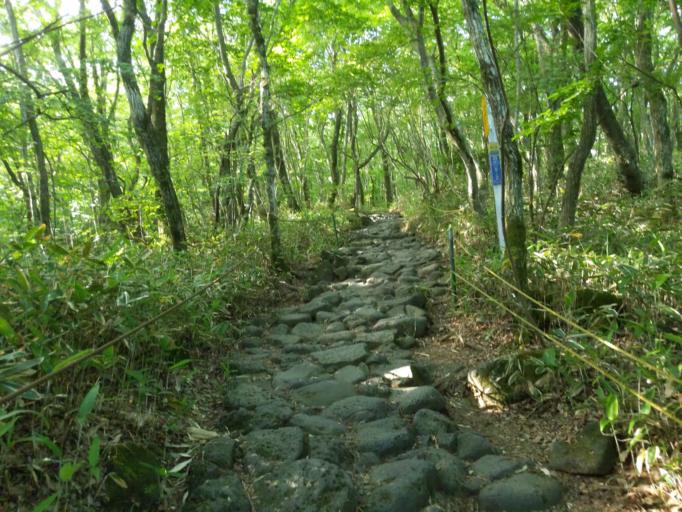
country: KR
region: Jeju-do
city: Jeju-si
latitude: 33.4178
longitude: 126.5481
